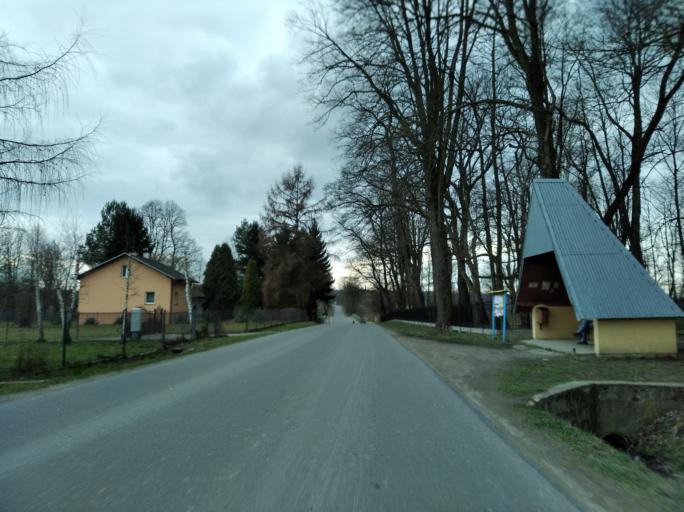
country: PL
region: Subcarpathian Voivodeship
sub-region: Powiat krosnienski
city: Odrzykon
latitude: 49.7556
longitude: 21.7165
